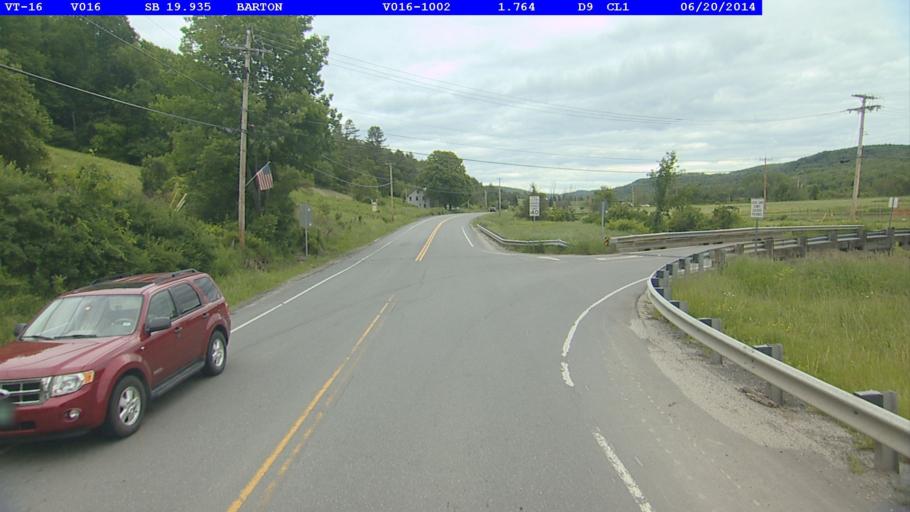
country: US
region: Vermont
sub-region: Orleans County
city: Newport
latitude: 44.7425
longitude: -72.1813
